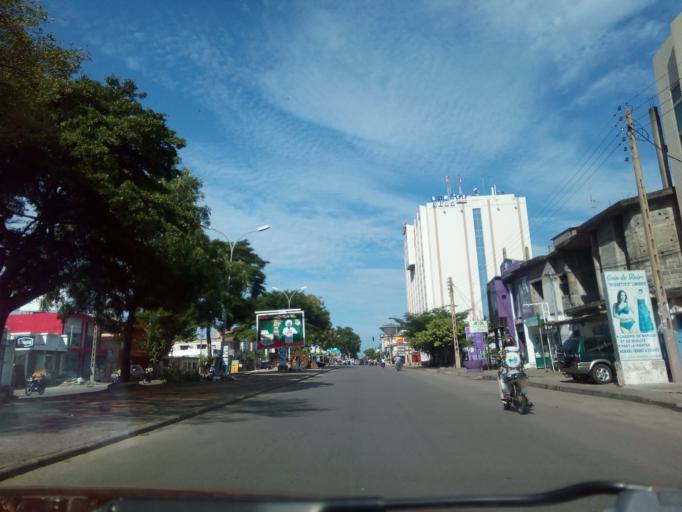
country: BJ
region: Littoral
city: Cotonou
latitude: 6.3649
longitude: 2.4270
